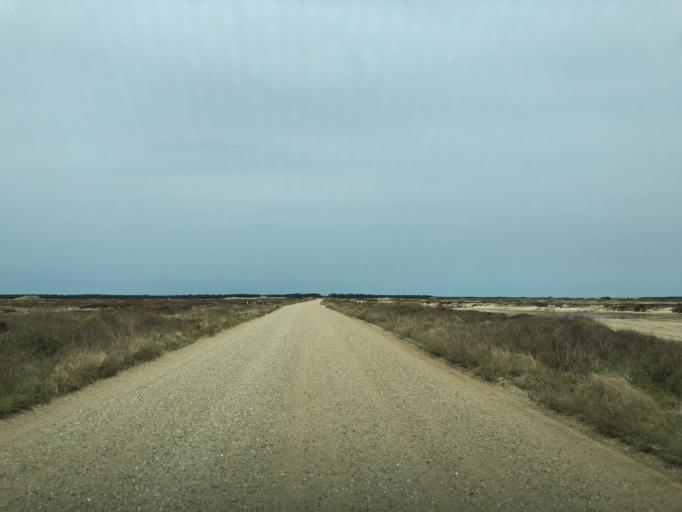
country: DK
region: South Denmark
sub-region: Varde Kommune
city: Oksbol
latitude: 55.5860
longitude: 8.1469
